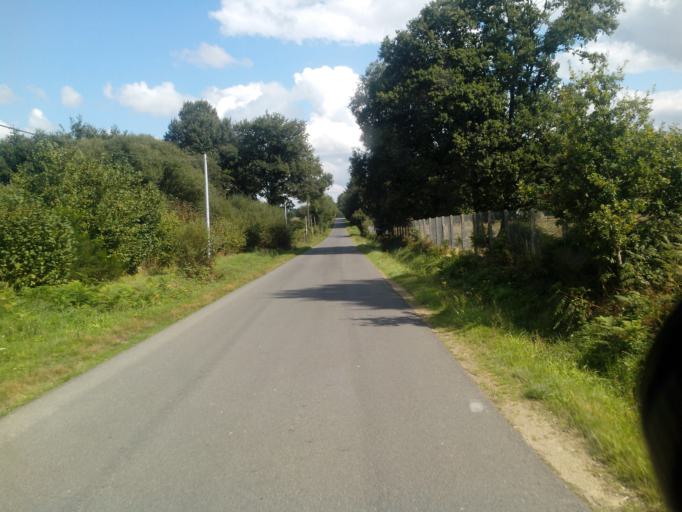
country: FR
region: Brittany
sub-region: Departement du Morbihan
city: Mauron
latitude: 48.1472
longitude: -2.3309
